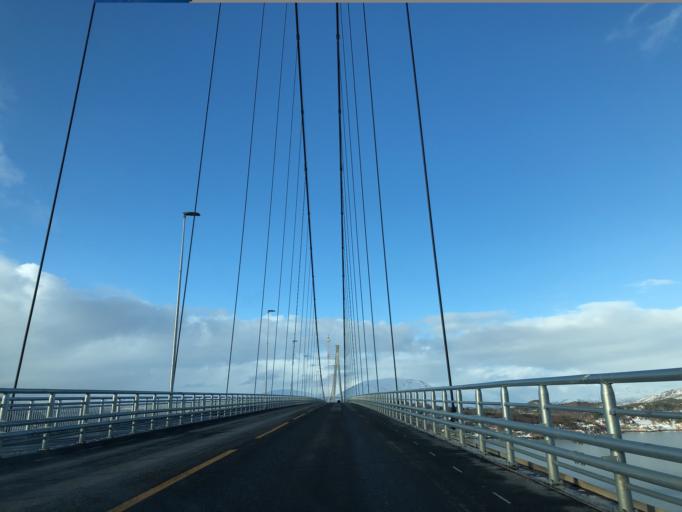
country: NO
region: Nordland
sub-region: Narvik
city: Narvik
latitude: 68.4548
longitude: 17.4815
